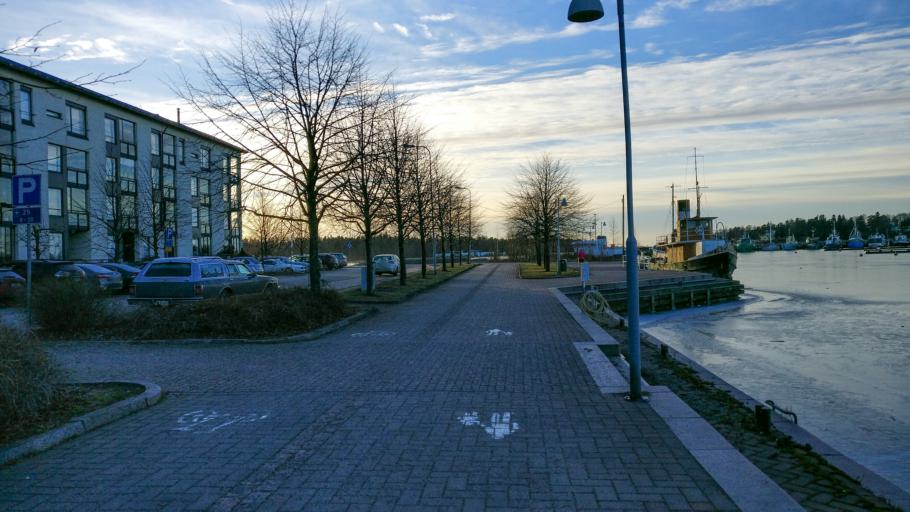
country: FI
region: Uusimaa
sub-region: Helsinki
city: Helsinki
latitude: 60.1865
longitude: 25.0296
